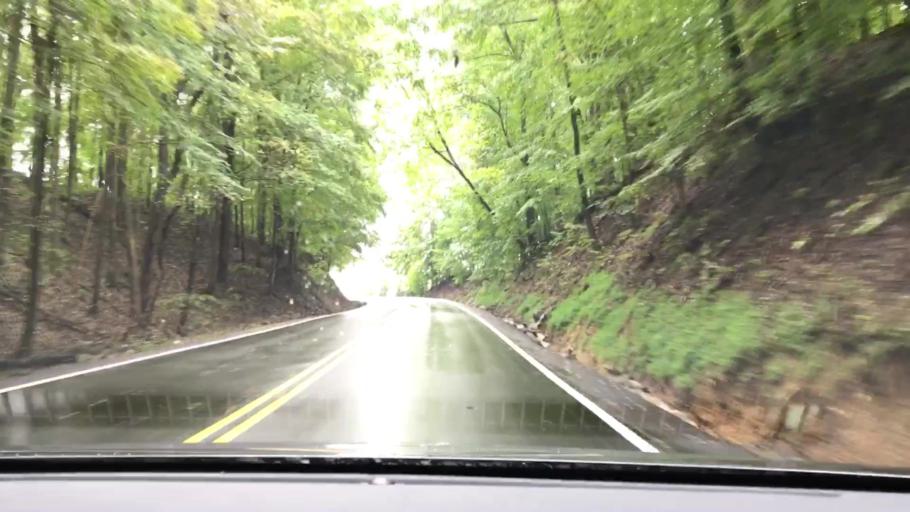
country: US
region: Tennessee
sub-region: Macon County
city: Red Boiling Springs
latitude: 36.4602
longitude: -85.8816
